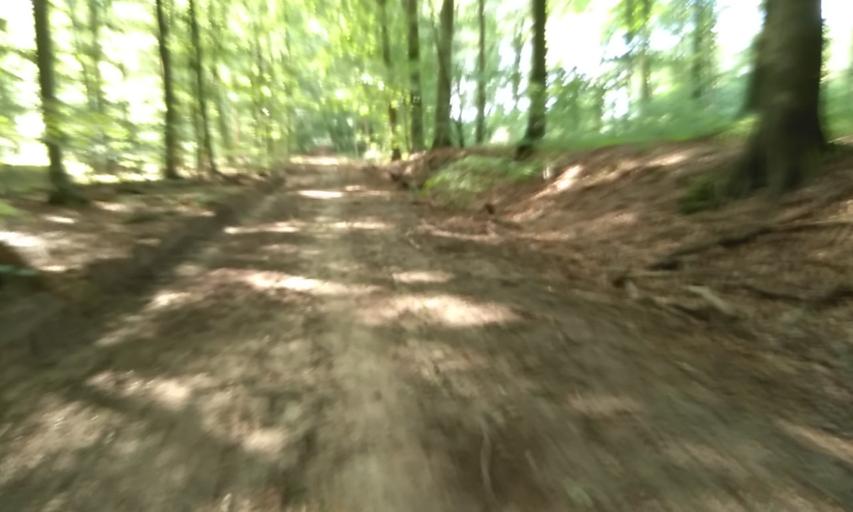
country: DE
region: Lower Saxony
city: Nottensdorf
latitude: 53.4767
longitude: 9.6419
